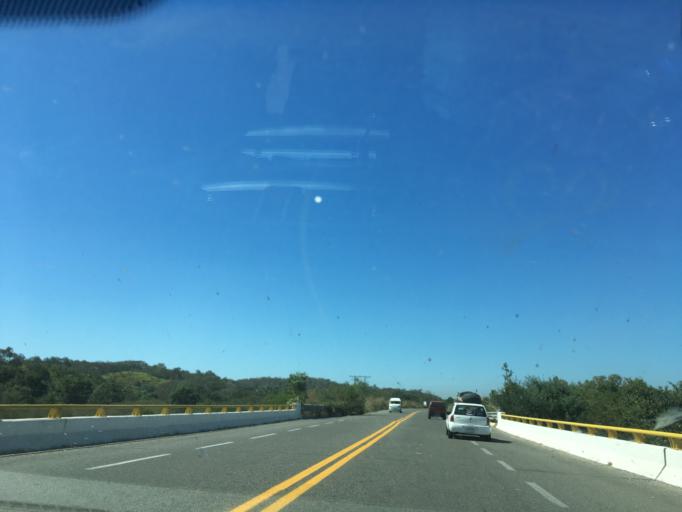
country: MX
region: Guerrero
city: La Union
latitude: 17.9757
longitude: -101.9191
